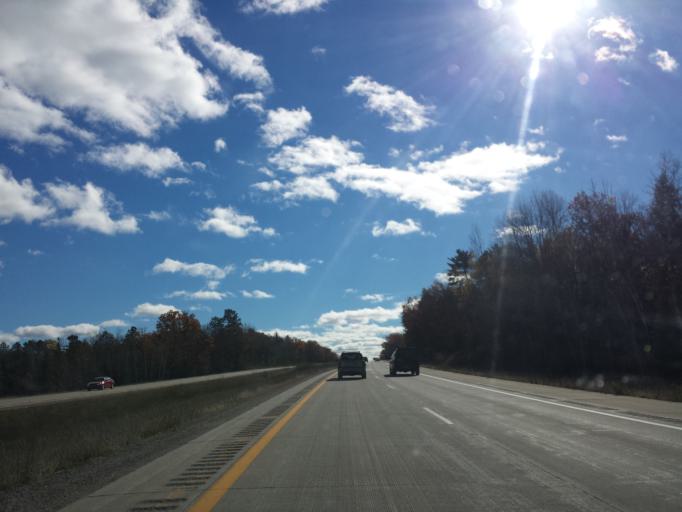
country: US
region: Michigan
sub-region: Cheboygan County
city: Indian River
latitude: 45.5346
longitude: -84.6160
